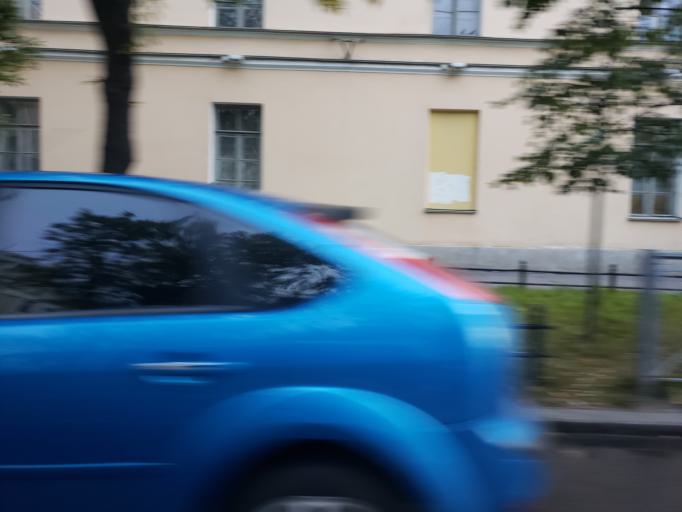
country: RU
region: St.-Petersburg
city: Vasyl'evsky Ostrov
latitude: 59.9350
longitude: 30.2779
